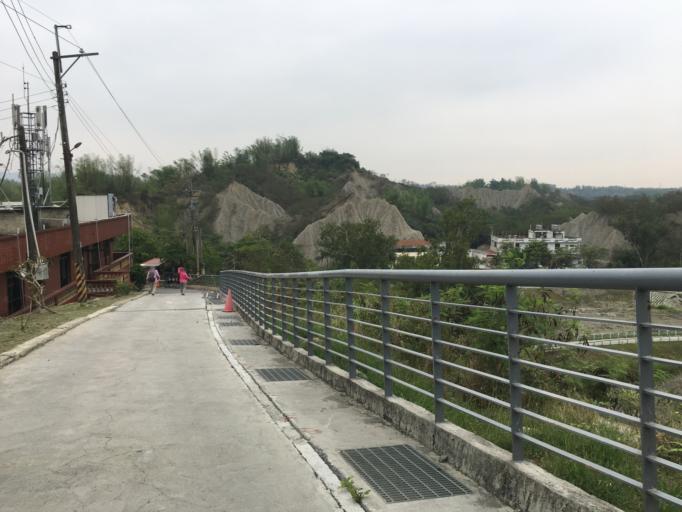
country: TW
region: Taiwan
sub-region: Tainan
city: Tainan
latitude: 22.8870
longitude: 120.3889
